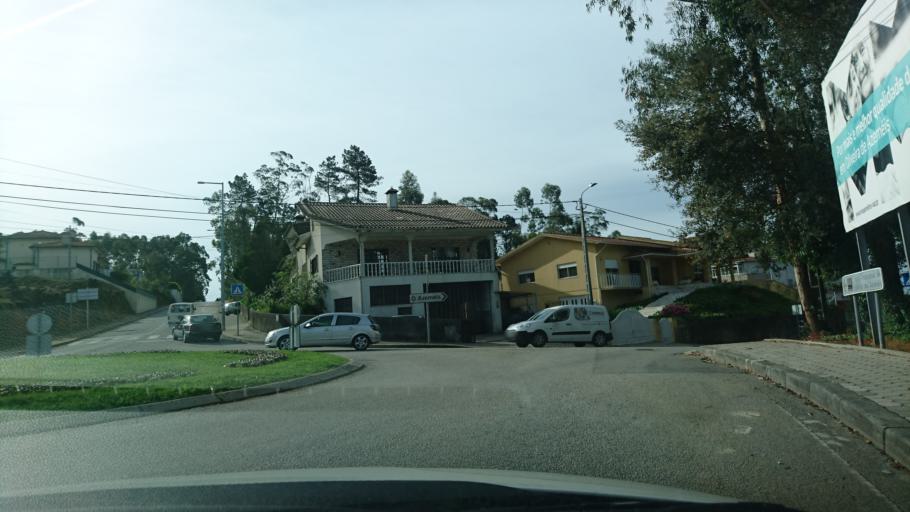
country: PT
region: Aveiro
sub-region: Oliveira de Azemeis
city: Vila Cha
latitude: 40.8603
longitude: -8.4725
